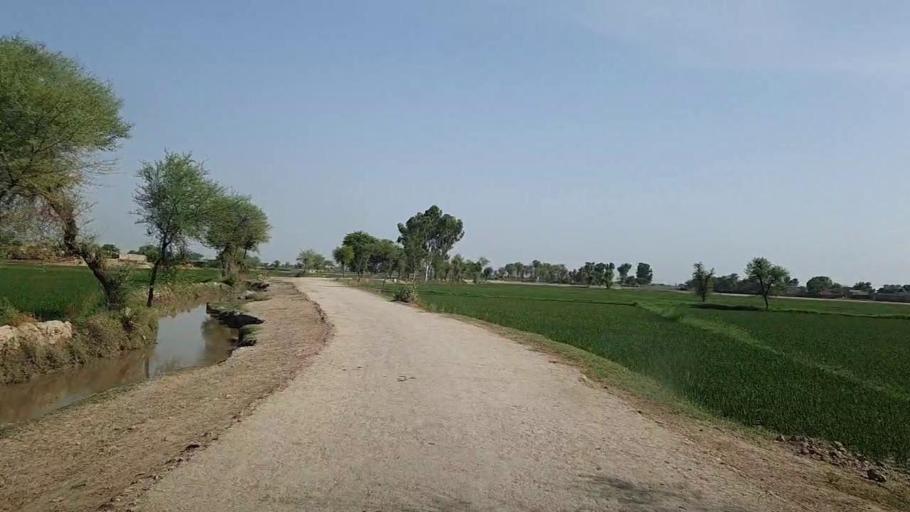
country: PK
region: Sindh
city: Sita Road
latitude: 27.0979
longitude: 67.8527
